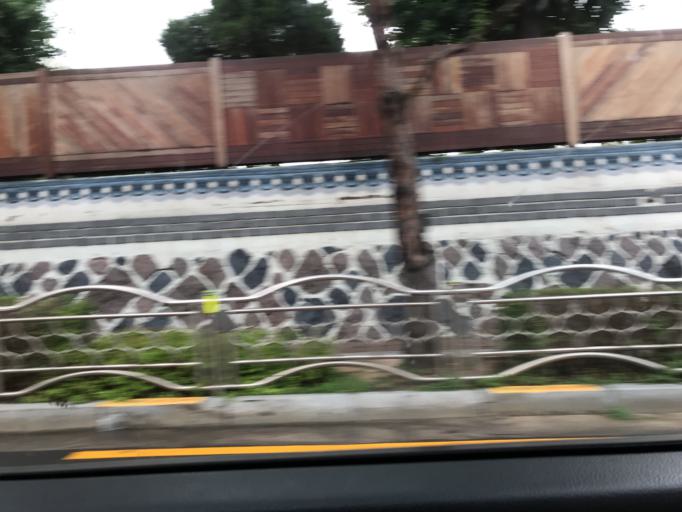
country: KR
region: Seoul
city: Seoul
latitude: 37.5795
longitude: 126.9850
